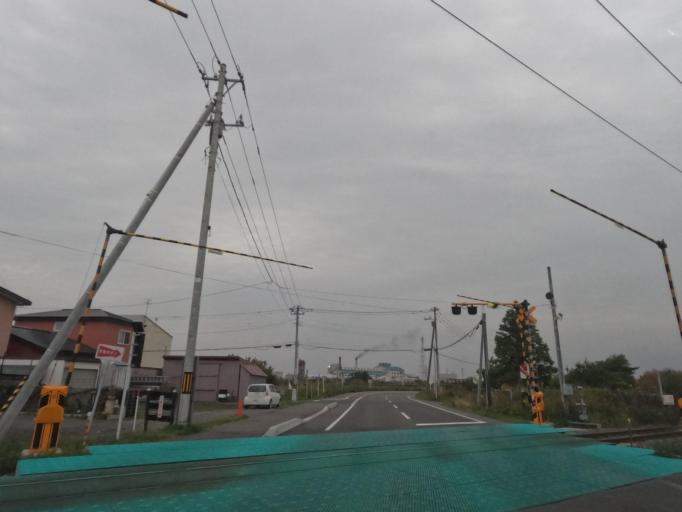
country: JP
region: Hokkaido
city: Date
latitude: 42.4754
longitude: 140.8490
